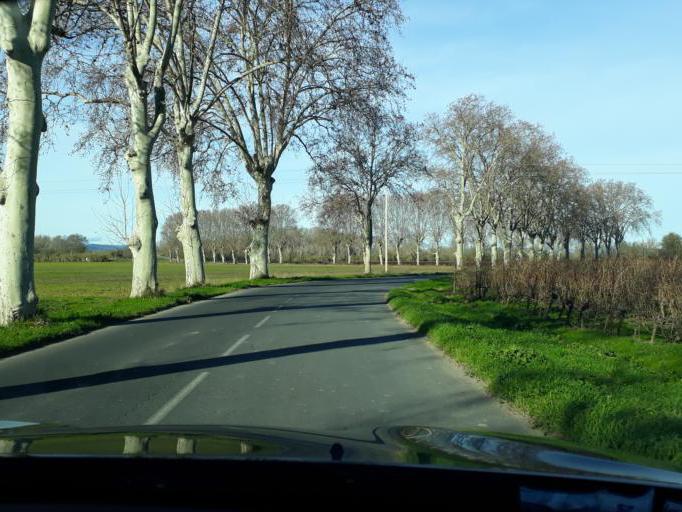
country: FR
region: Languedoc-Roussillon
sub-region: Departement de l'Herault
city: Castelnau-de-Guers
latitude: 43.4442
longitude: 3.4402
